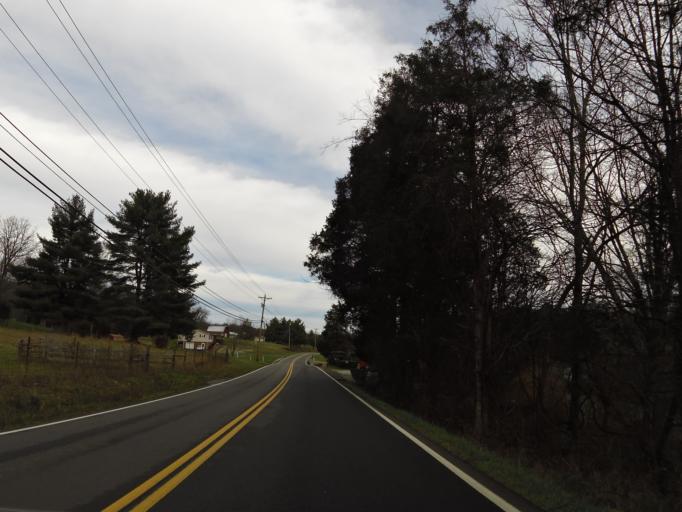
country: US
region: Tennessee
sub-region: Greene County
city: Mosheim
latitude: 36.1029
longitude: -82.9240
